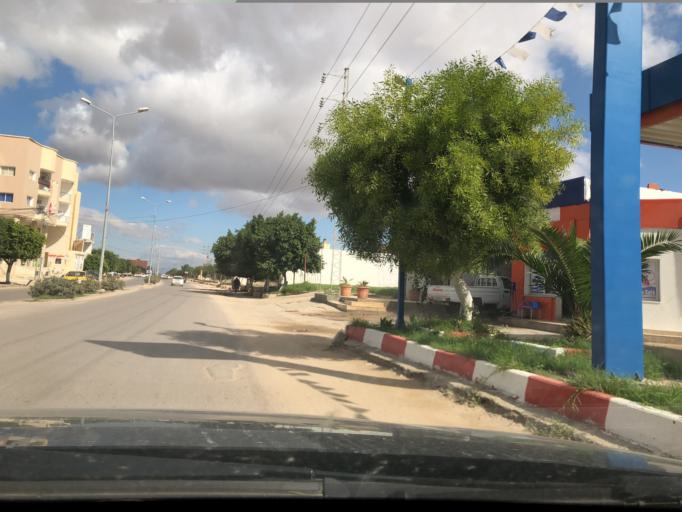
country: TN
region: Al Qasrayn
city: Kasserine
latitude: 35.1736
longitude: 8.8457
